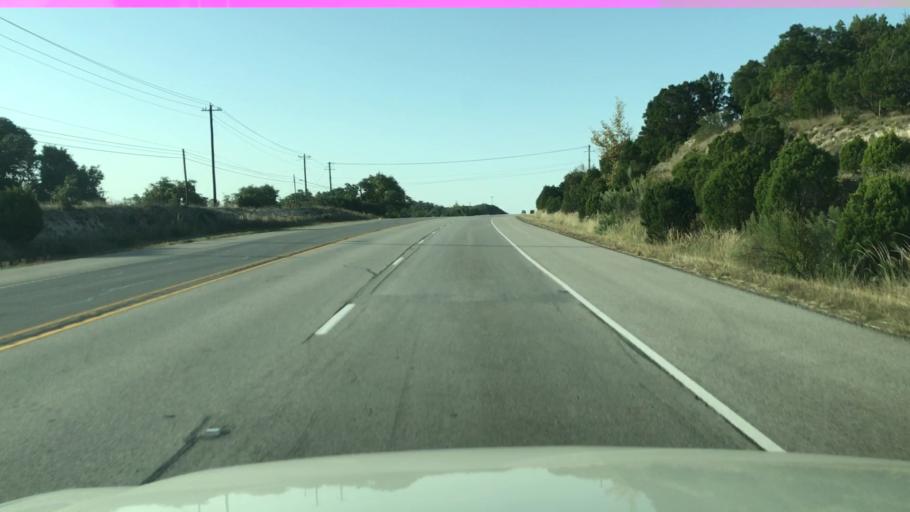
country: US
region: Texas
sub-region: Blanco County
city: Blanco
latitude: 30.1767
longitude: -98.3801
